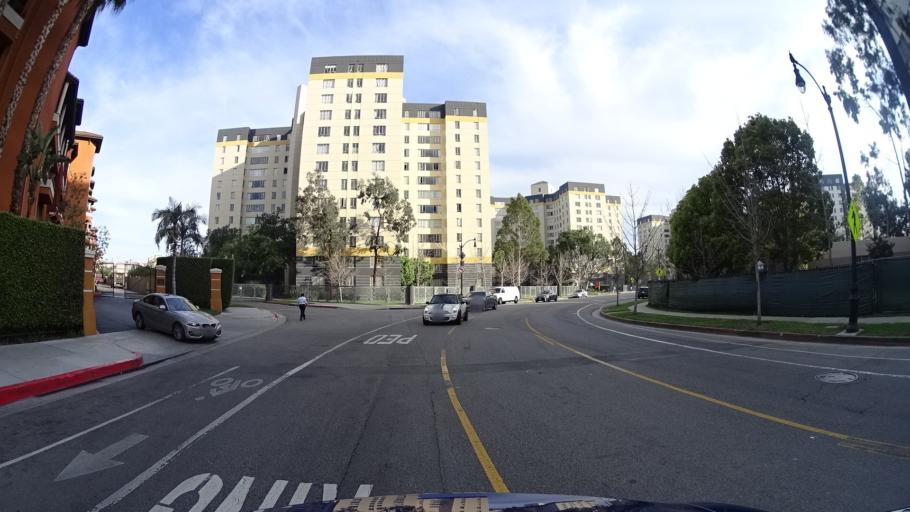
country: US
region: California
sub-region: Los Angeles County
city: West Hollywood
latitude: 34.0684
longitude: -118.3501
